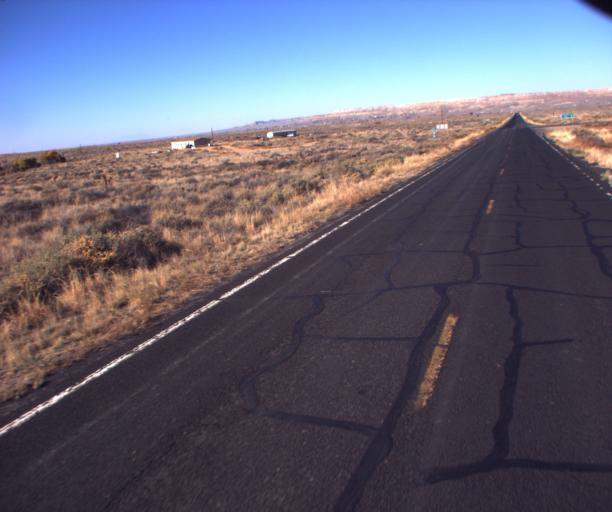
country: US
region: Arizona
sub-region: Navajo County
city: First Mesa
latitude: 35.8390
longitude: -110.3063
